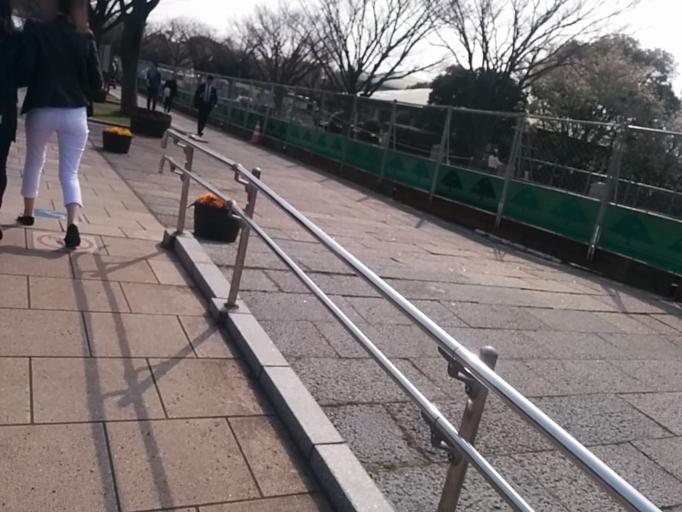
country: JP
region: Tokyo
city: Urayasu
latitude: 35.6434
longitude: 139.8611
